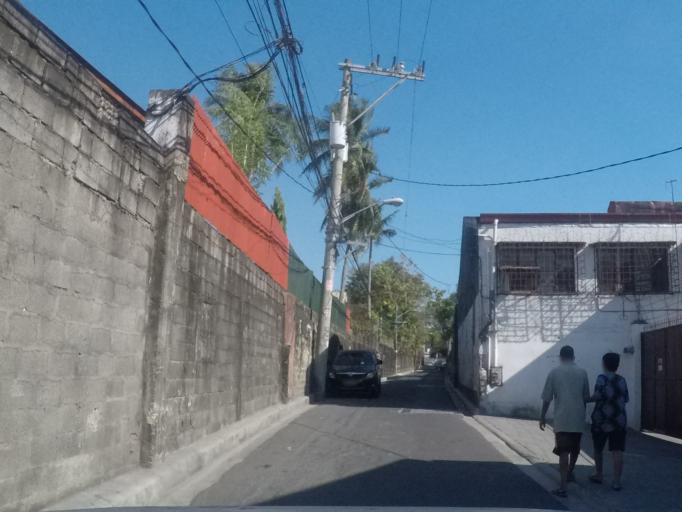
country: PH
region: Metro Manila
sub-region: San Juan
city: San Juan
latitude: 14.6070
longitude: 121.0296
